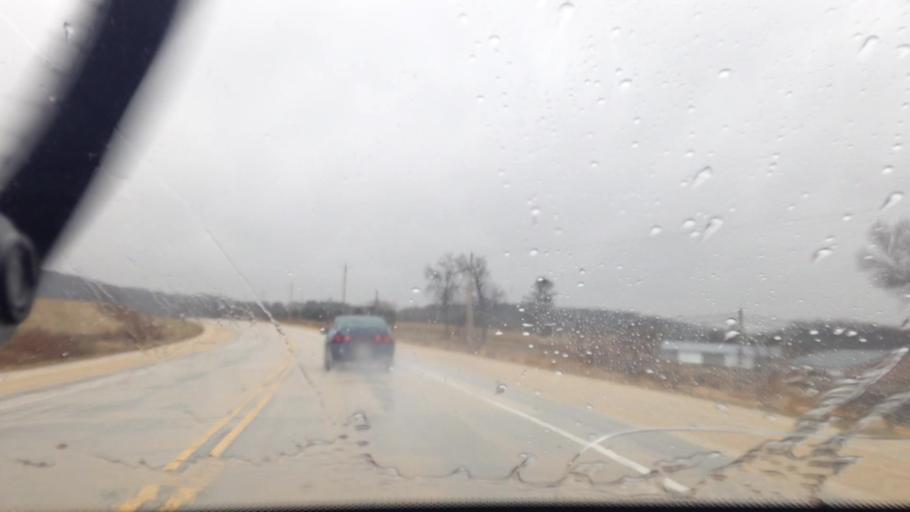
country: US
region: Wisconsin
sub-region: Dodge County
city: Mayville
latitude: 43.4655
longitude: -88.5463
